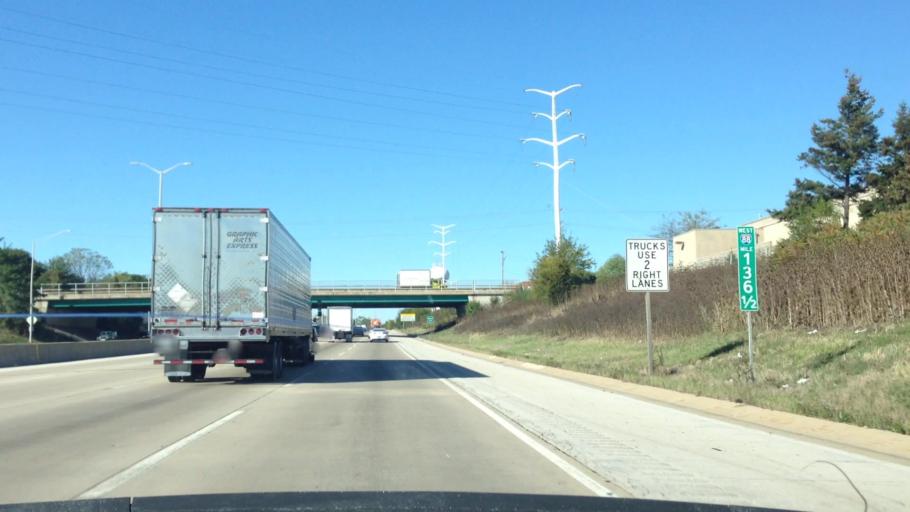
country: US
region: Illinois
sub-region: DuPage County
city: Oakbrook Terrace
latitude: 41.8447
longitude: -87.9703
